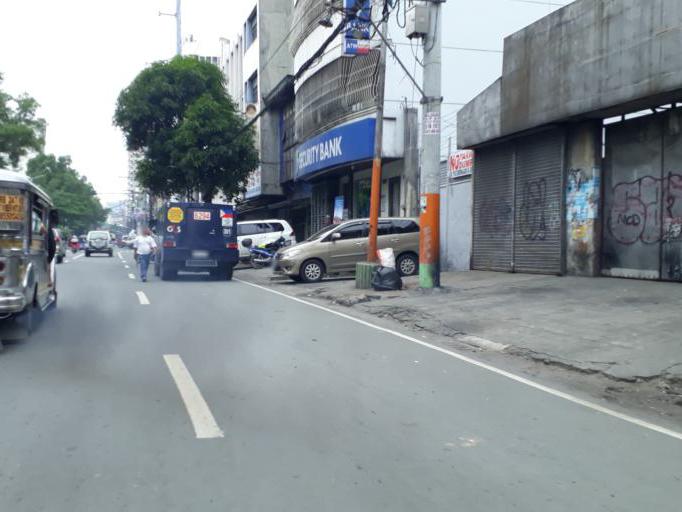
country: PH
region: Metro Manila
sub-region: City of Manila
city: Manila
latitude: 14.6162
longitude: 120.9771
